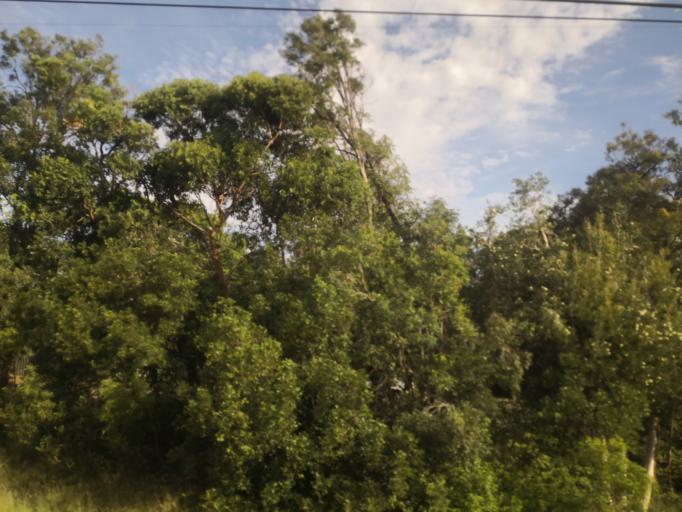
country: AU
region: New South Wales
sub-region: Gosford Shire
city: Blackwall
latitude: -33.4968
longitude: 151.3075
